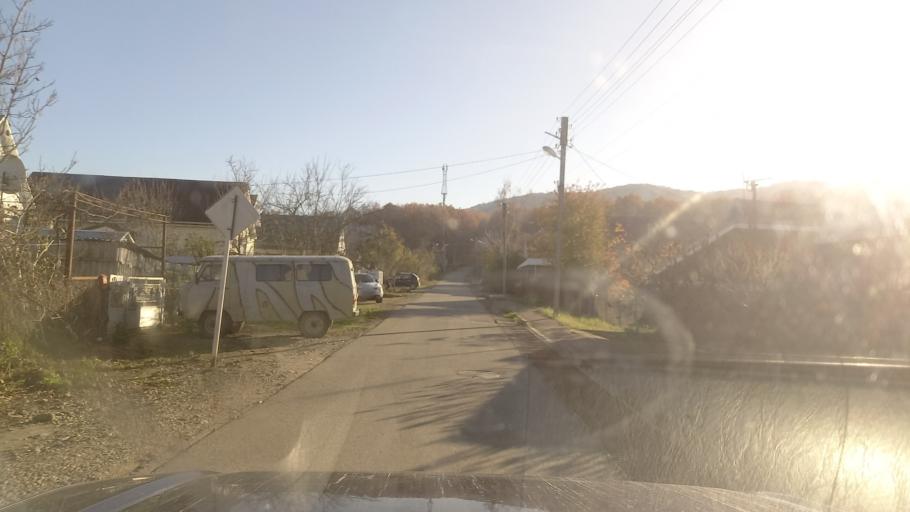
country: RU
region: Krasnodarskiy
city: Goryachiy Klyuch
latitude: 44.6197
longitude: 39.1043
